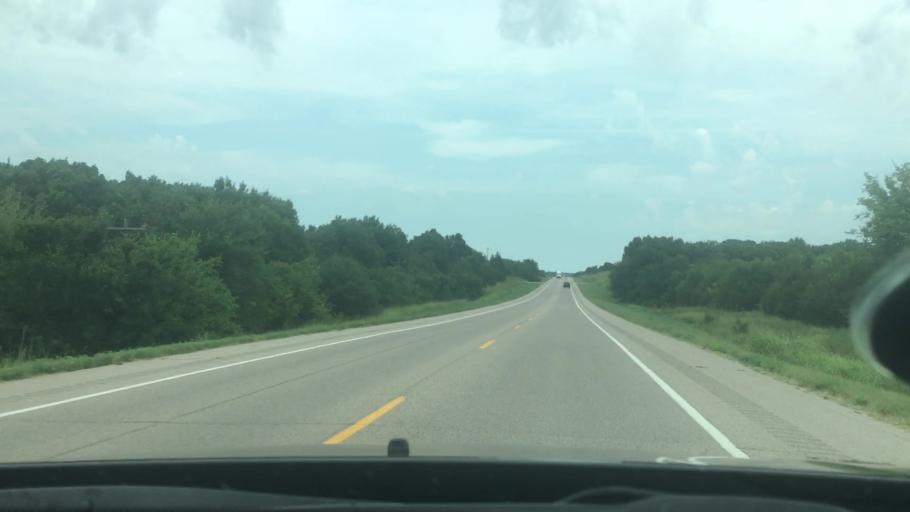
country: US
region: Oklahoma
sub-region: Seminole County
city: Konawa
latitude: 34.9892
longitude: -96.6792
